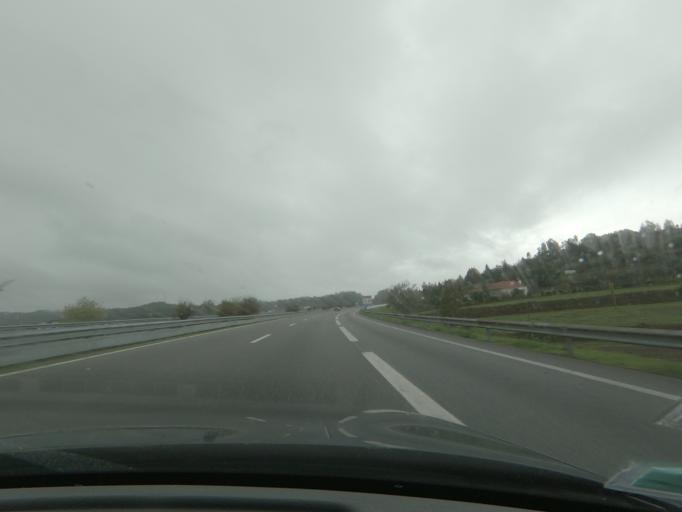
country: PT
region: Porto
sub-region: Lousada
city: Meinedo
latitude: 41.2322
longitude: -8.2120
